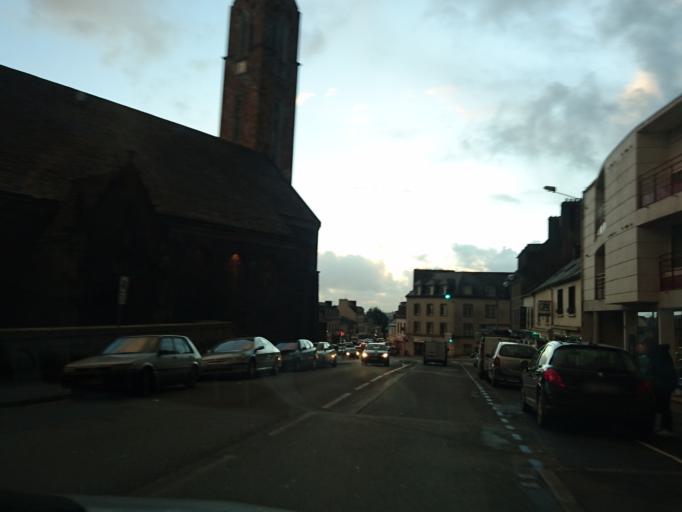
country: FR
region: Brittany
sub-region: Departement du Finistere
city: Guipavas
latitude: 48.4348
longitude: -4.4010
